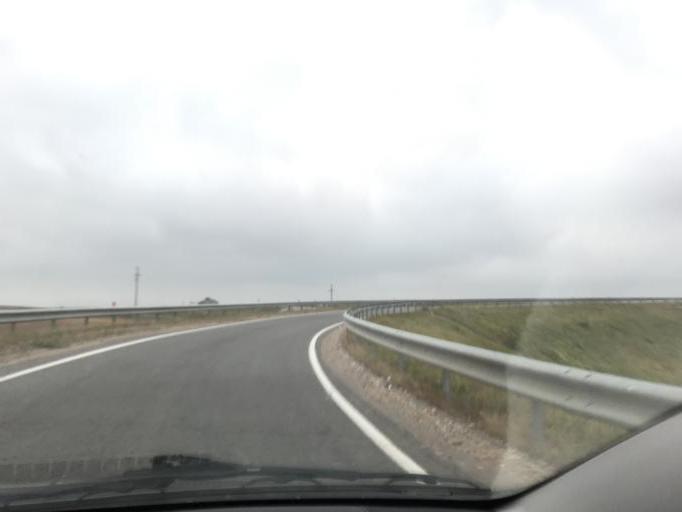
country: BY
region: Vitebsk
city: Vitebsk
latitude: 55.1549
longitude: 30.0675
